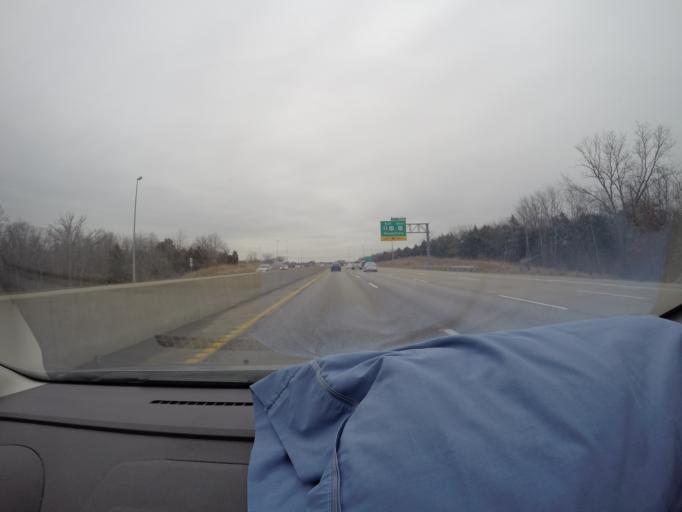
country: US
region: Missouri
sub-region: Saint Charles County
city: Wentzville
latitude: 38.8059
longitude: -90.8485
